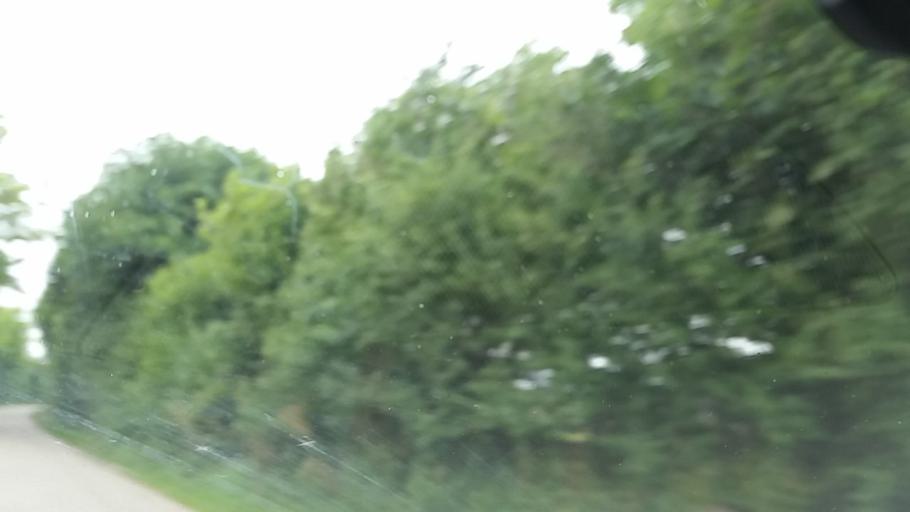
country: DE
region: Schleswig-Holstein
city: Dannewerk
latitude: 54.4918
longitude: 9.5000
